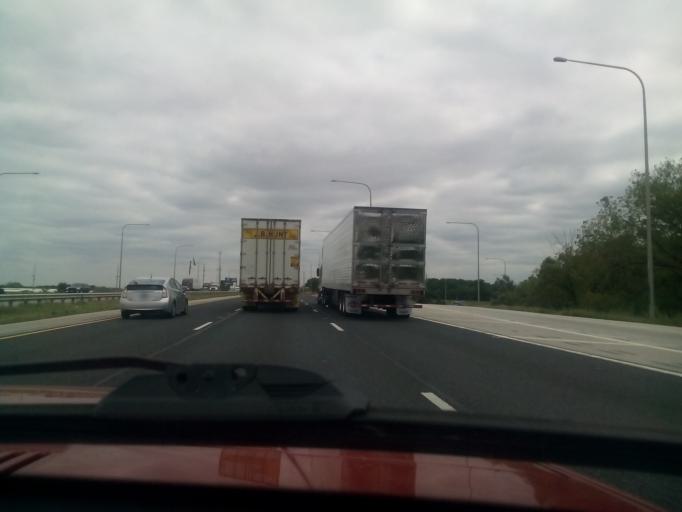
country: US
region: Illinois
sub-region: Cook County
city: Markham
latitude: 41.5829
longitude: -87.6984
